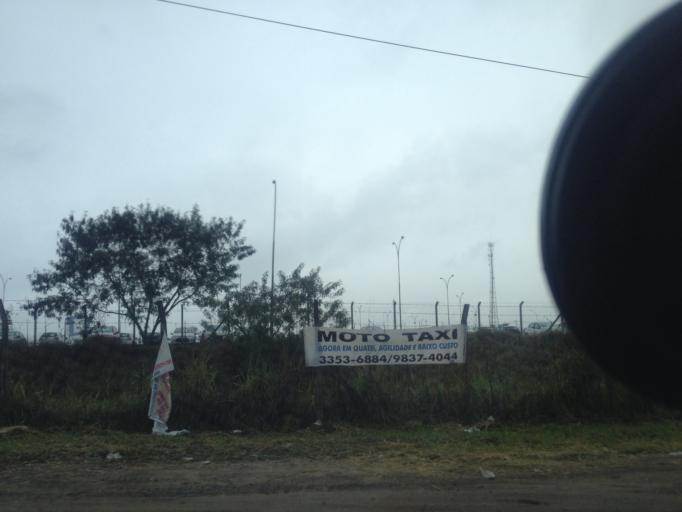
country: BR
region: Rio de Janeiro
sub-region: Porto Real
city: Porto Real
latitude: -22.4211
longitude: -44.3495
